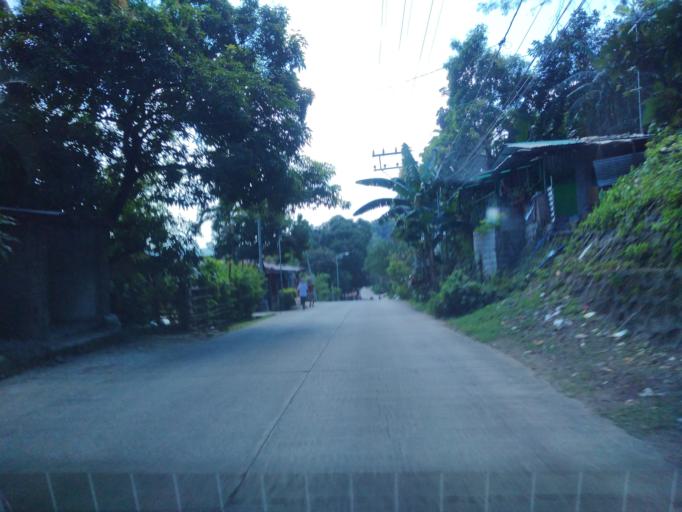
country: PH
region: Central Luzon
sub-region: Province of Bulacan
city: San Jose del Monte
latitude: 14.8470
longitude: 121.0716
